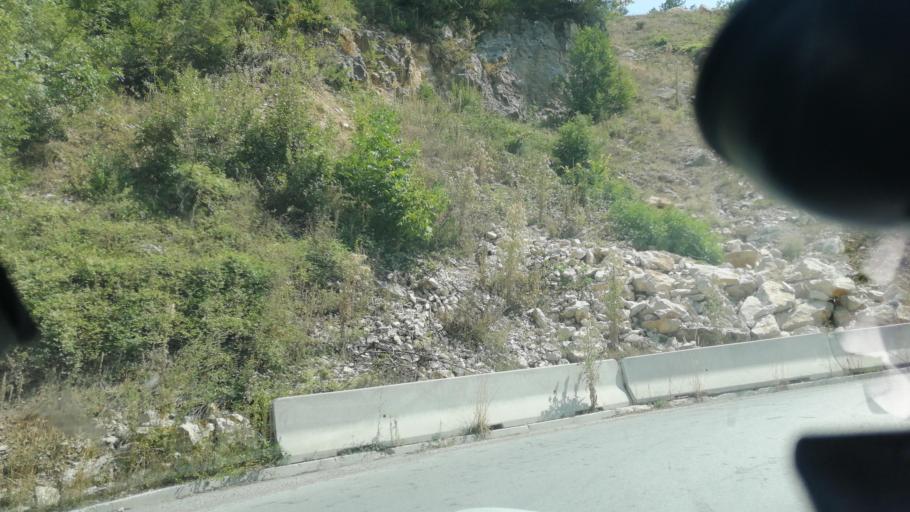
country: RS
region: Central Serbia
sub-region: Moravicki Okrug
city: Ivanjica
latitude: 43.6261
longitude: 20.2416
